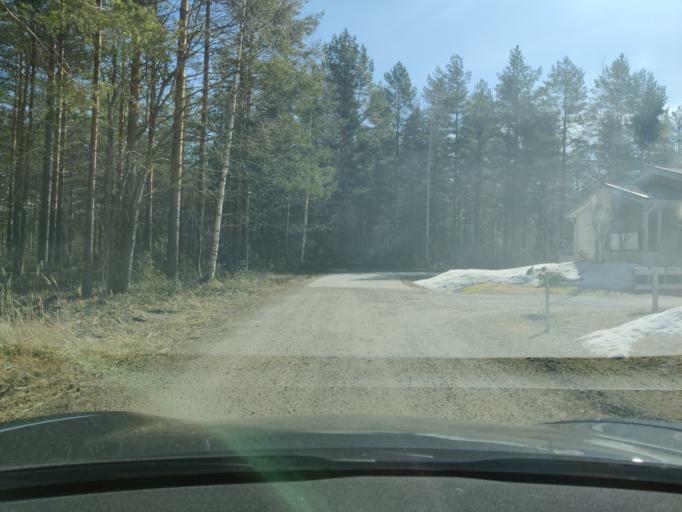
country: FI
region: Northern Savo
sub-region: Kuopio
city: Vehmersalmi
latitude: 62.7690
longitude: 27.9918
